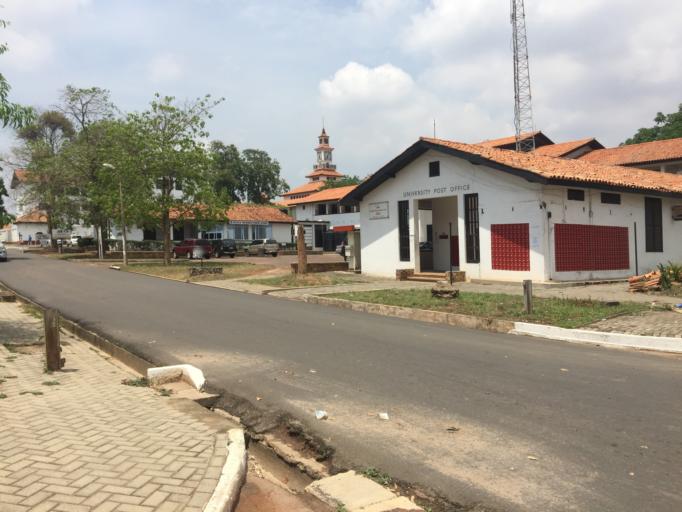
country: GH
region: Greater Accra
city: Medina Estates
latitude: 5.6507
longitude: -0.1879
